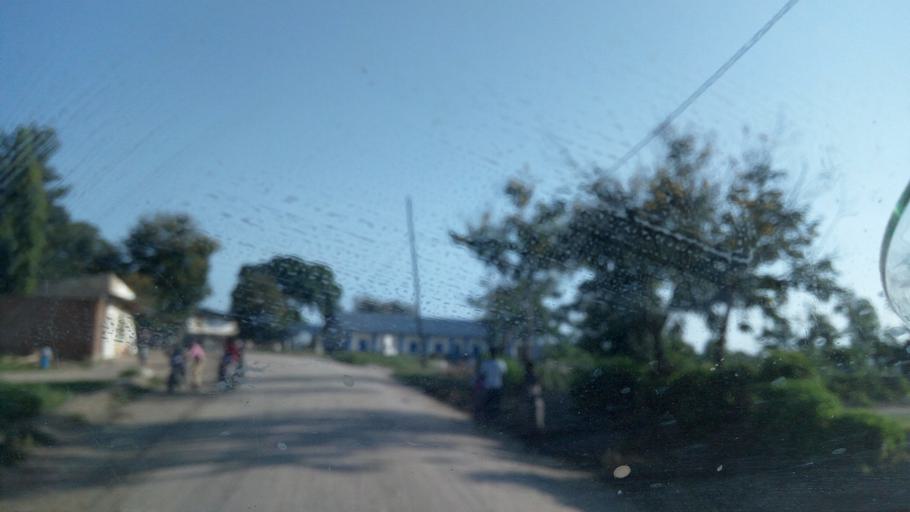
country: BI
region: Bururi
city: Rumonge
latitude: -4.1005
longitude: 29.0936
